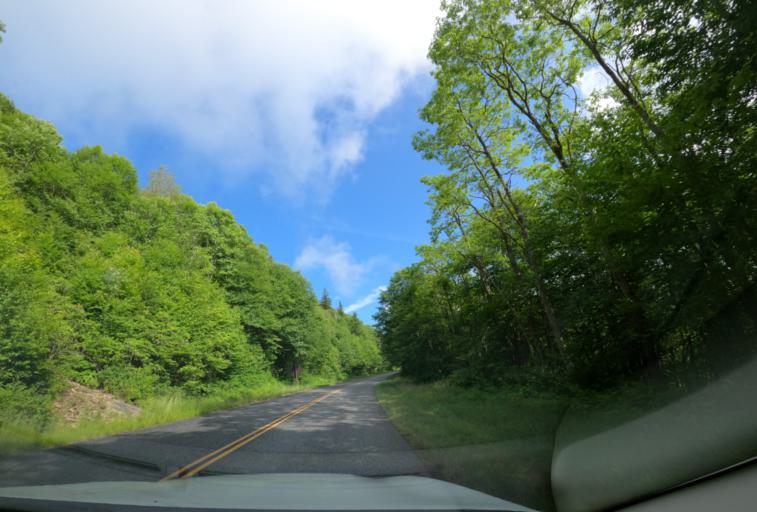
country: US
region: North Carolina
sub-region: Haywood County
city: Hazelwood
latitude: 35.3181
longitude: -82.9625
